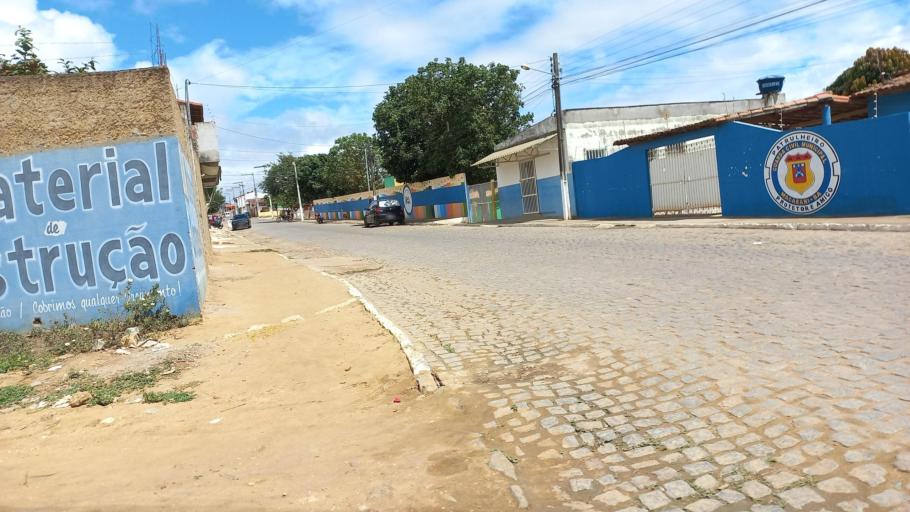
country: BR
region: Bahia
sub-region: Itapetinga
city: Itapetinga
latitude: -15.5719
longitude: -40.4326
